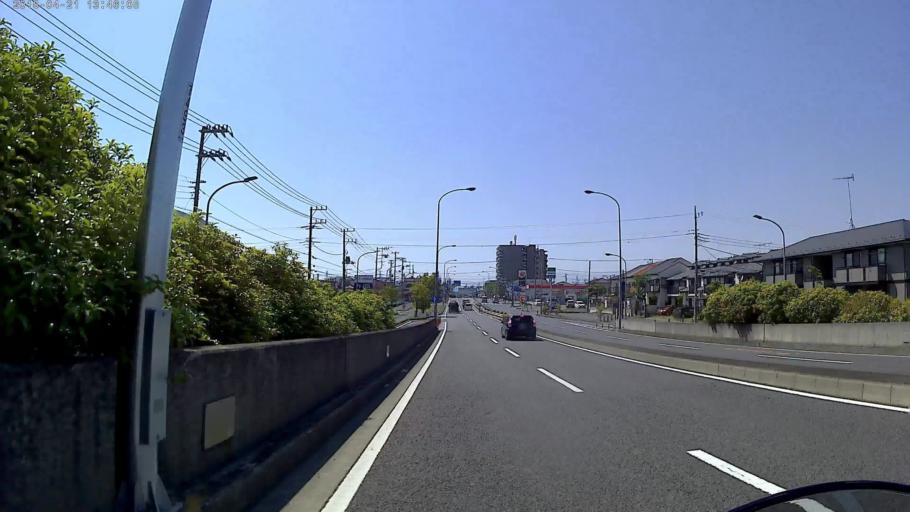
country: JP
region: Kanagawa
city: Hiratsuka
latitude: 35.3540
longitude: 139.3655
